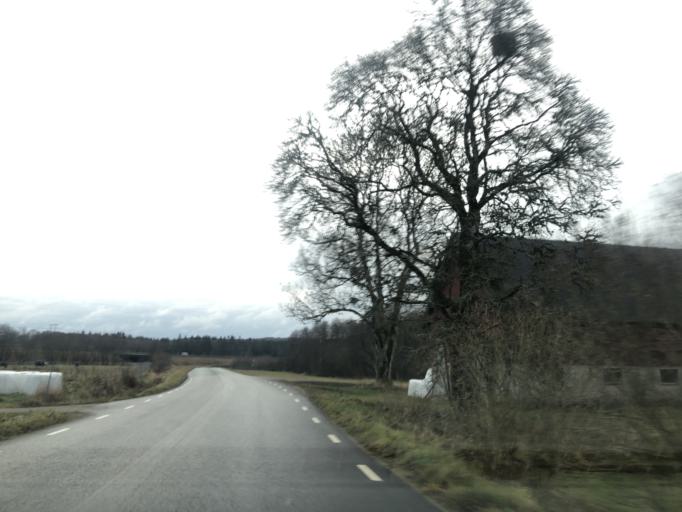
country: SE
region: Vaestra Goetaland
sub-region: Ulricehamns Kommun
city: Ulricehamn
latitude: 57.8123
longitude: 13.2418
